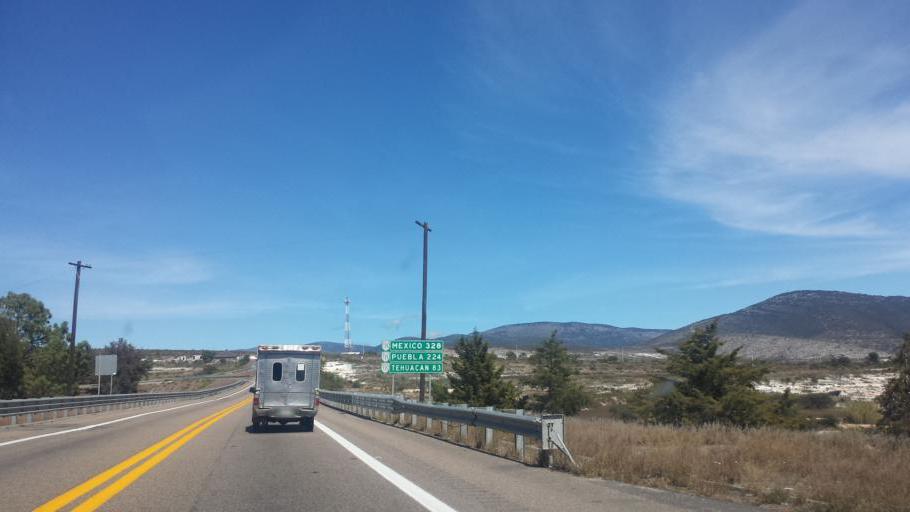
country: MX
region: Oaxaca
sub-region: Villa Tejupam de la Union
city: Villa Tejupam de la Union
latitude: 17.8861
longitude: -97.3729
